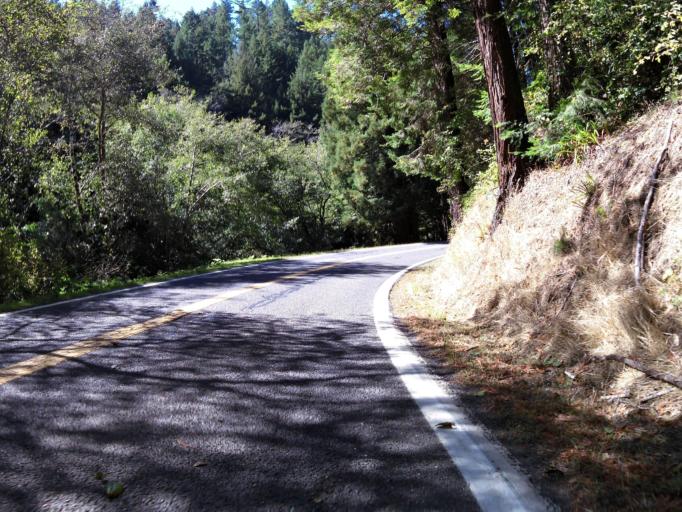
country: US
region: California
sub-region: Mendocino County
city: Fort Bragg
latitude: 39.7800
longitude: -123.8253
